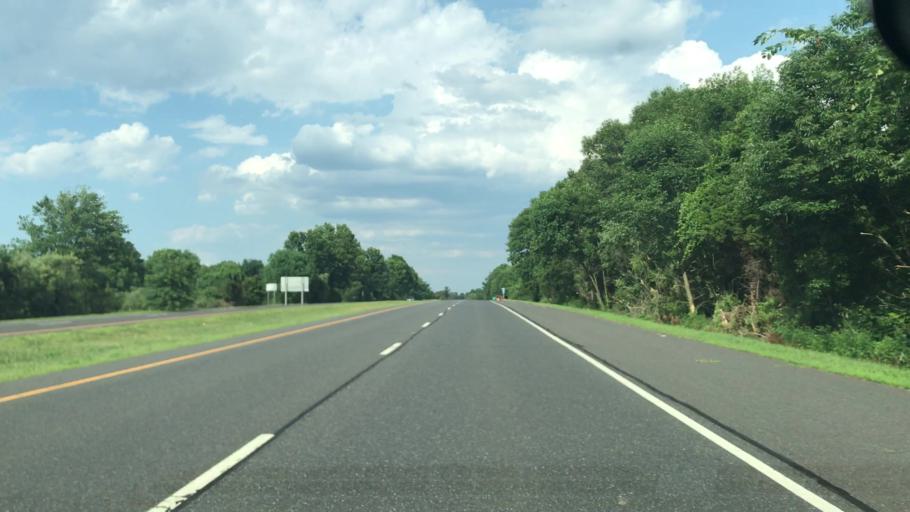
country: US
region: New Jersey
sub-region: Hunterdon County
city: Lambertville
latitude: 40.4117
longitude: -74.8961
